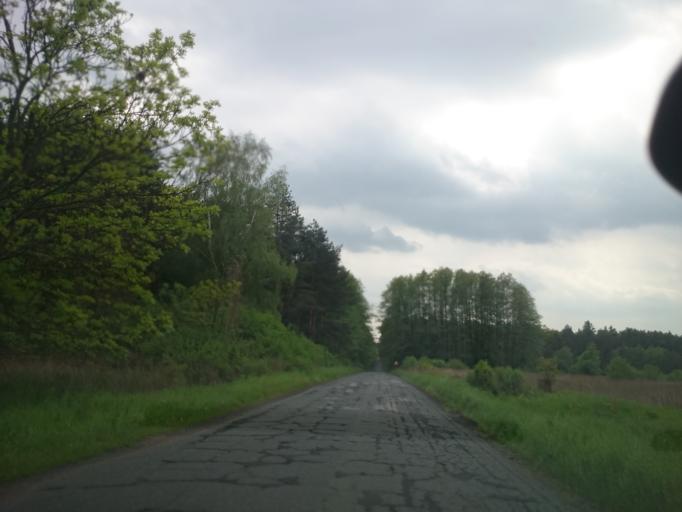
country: PL
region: Lower Silesian Voivodeship
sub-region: Powiat olesnicki
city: Dobroszyce
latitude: 51.3527
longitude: 17.2760
